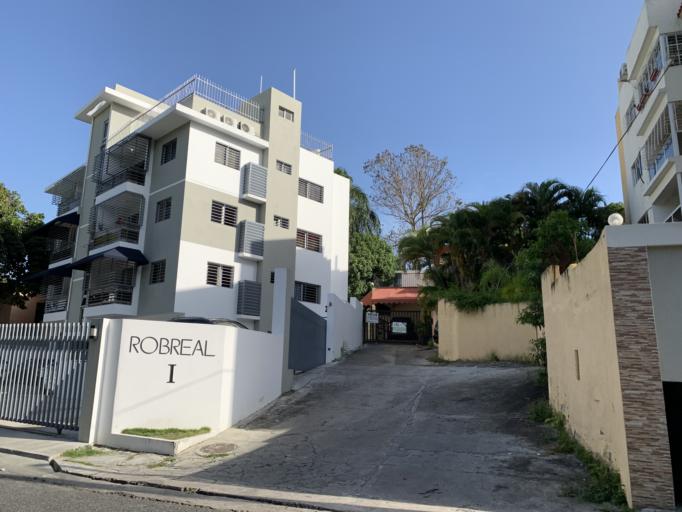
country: DO
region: Nacional
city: Santo Domingo
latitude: 18.4842
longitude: -69.9691
